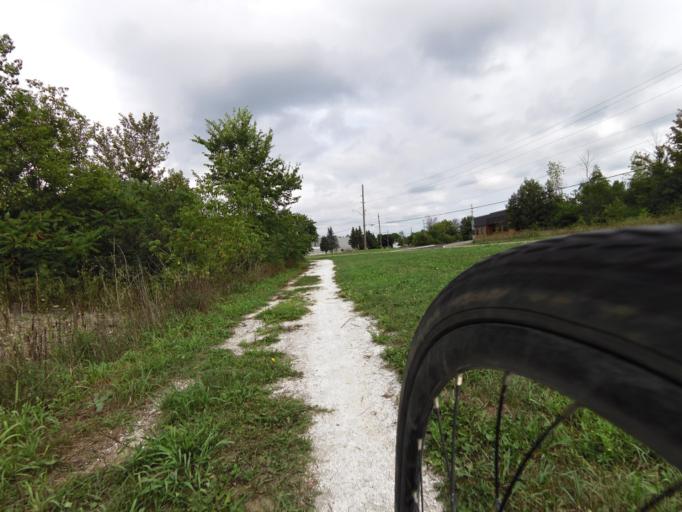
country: CA
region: Ontario
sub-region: Lanark County
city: Smiths Falls
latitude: 44.8908
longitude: -76.0265
